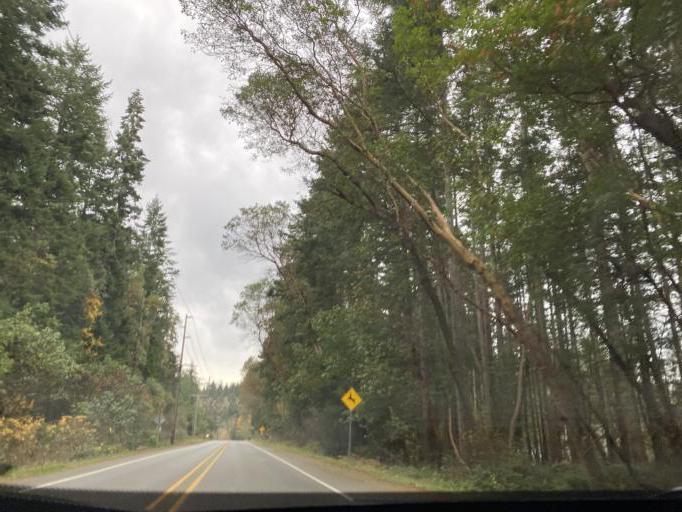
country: US
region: Washington
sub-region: Island County
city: Freeland
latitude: 48.0170
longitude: -122.5816
